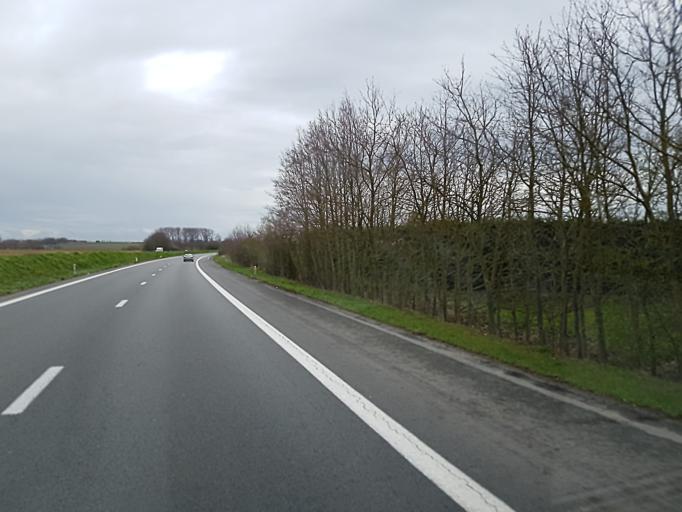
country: BE
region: Wallonia
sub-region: Province du Hainaut
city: Estaimpuis
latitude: 50.7618
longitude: 3.2865
